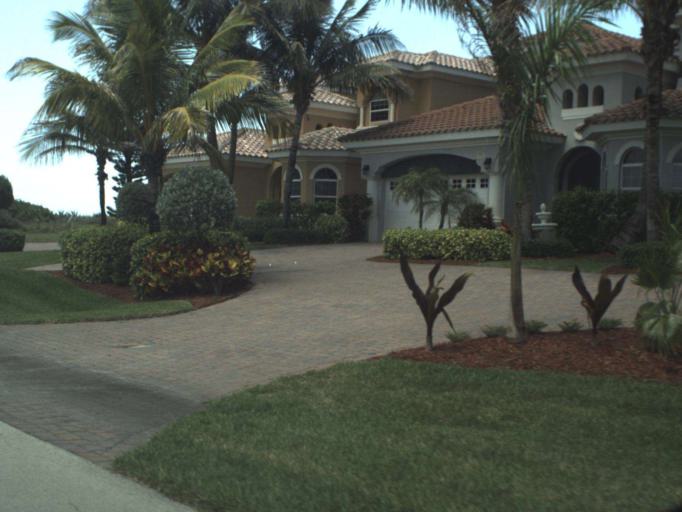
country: US
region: Florida
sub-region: Brevard County
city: Malabar
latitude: 27.9739
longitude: -80.5116
